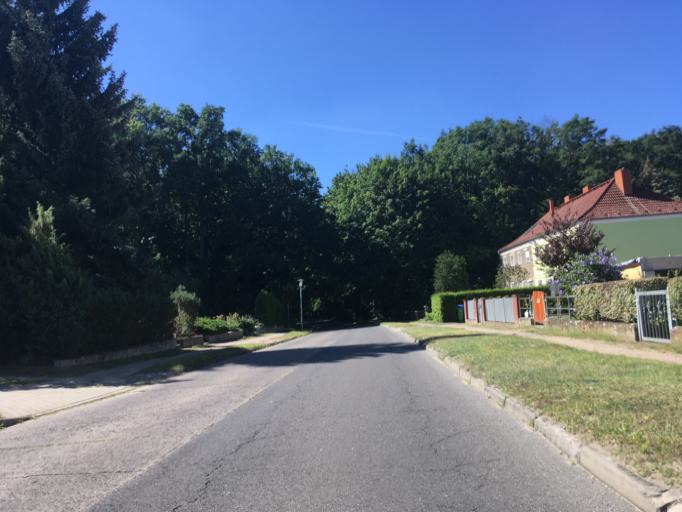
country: DE
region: Brandenburg
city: Woltersdorf
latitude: 52.4615
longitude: 13.7792
